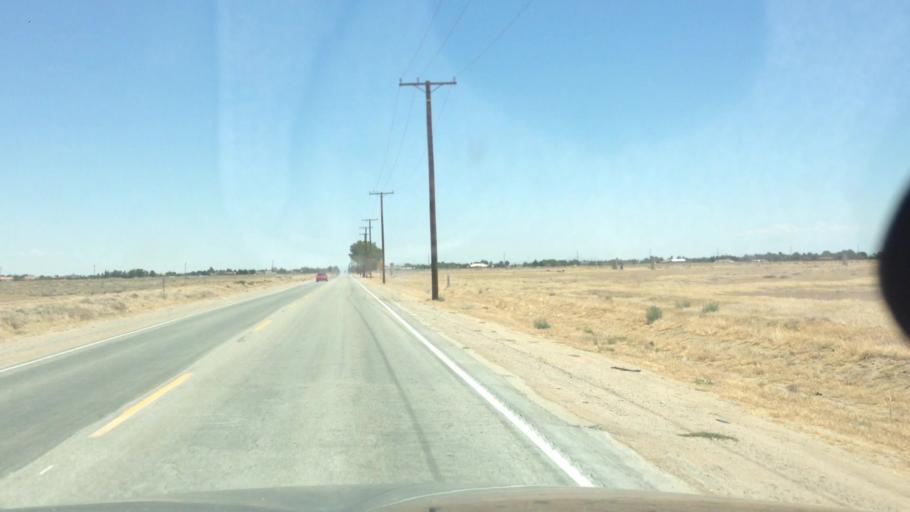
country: US
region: California
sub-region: Los Angeles County
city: Quartz Hill
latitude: 34.7764
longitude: -118.3017
